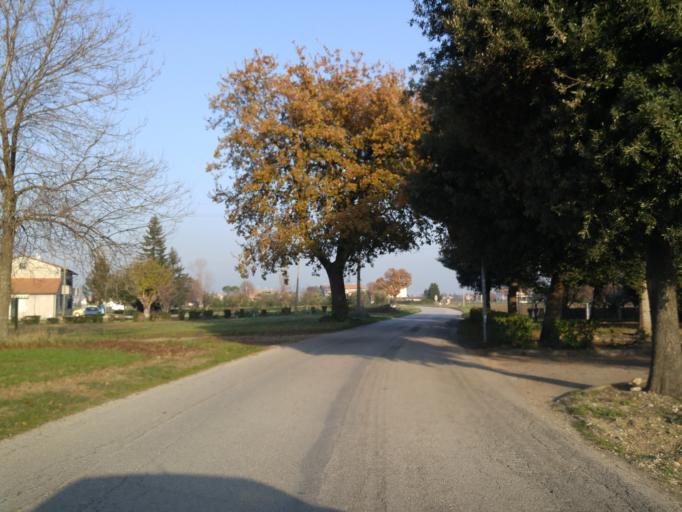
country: IT
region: The Marches
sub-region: Provincia di Pesaro e Urbino
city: Bellocchi
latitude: 43.7907
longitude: 12.9883
